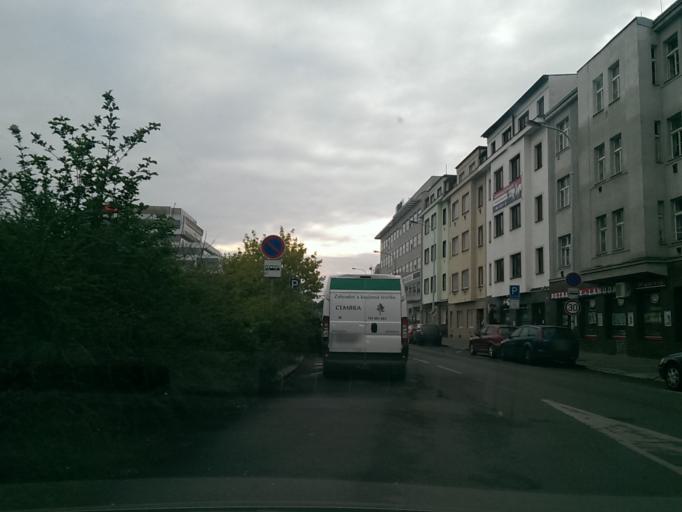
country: CZ
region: Praha
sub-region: Praha 2
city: Vysehrad
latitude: 50.0605
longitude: 14.4279
